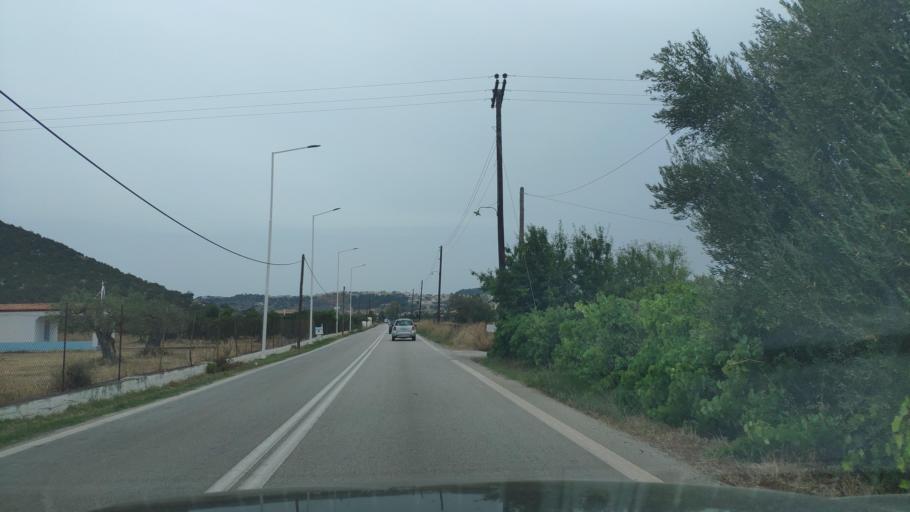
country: GR
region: Peloponnese
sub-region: Nomos Argolidos
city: Kranidi
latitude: 37.4011
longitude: 23.1555
